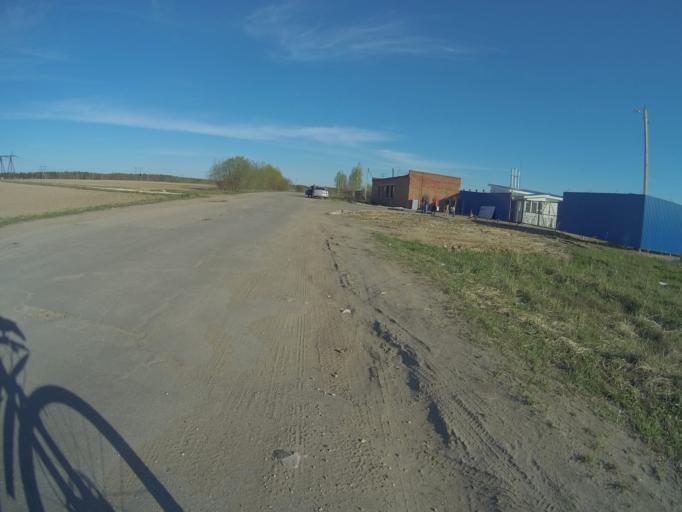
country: RU
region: Vladimir
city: Kommunar
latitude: 56.0545
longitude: 40.4851
